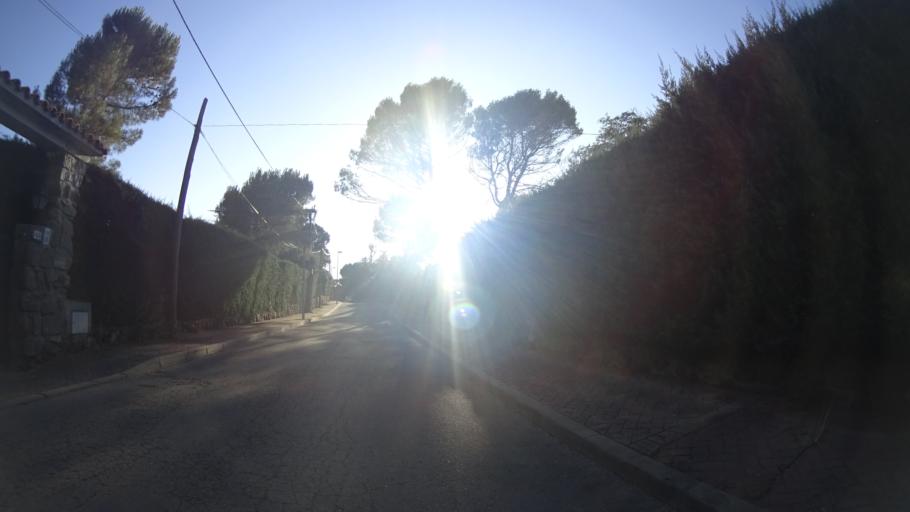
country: ES
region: Madrid
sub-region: Provincia de Madrid
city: Galapagar
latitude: 40.5668
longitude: -3.9999
